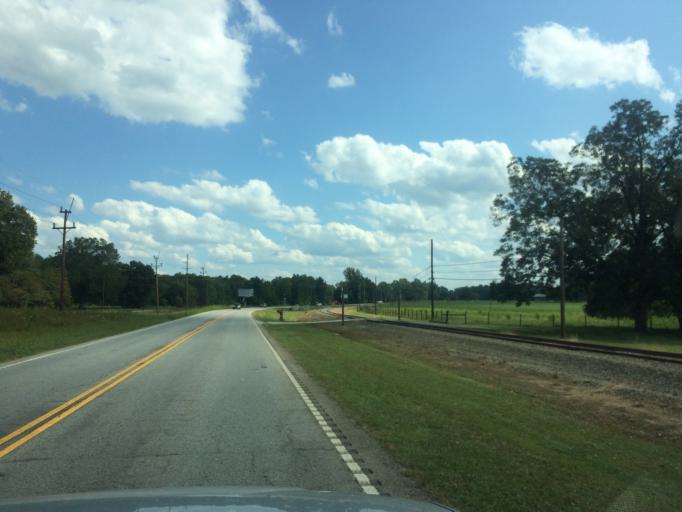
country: US
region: South Carolina
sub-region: Anderson County
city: Belton
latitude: 34.4963
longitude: -82.4608
